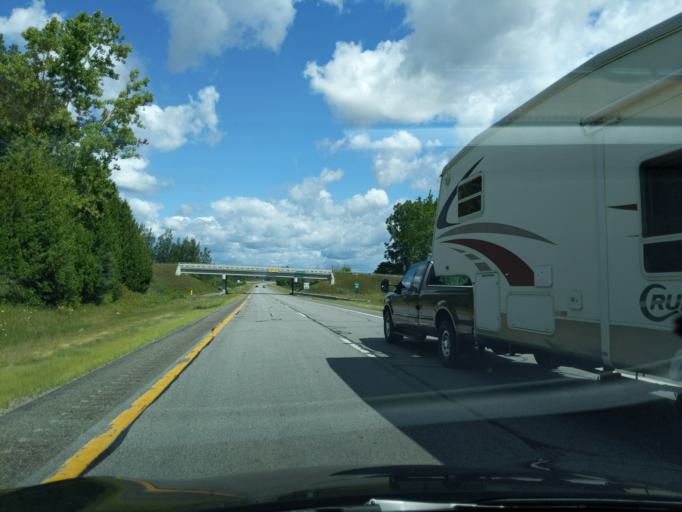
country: US
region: Michigan
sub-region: Clare County
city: Clare
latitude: 43.7555
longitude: -84.7573
